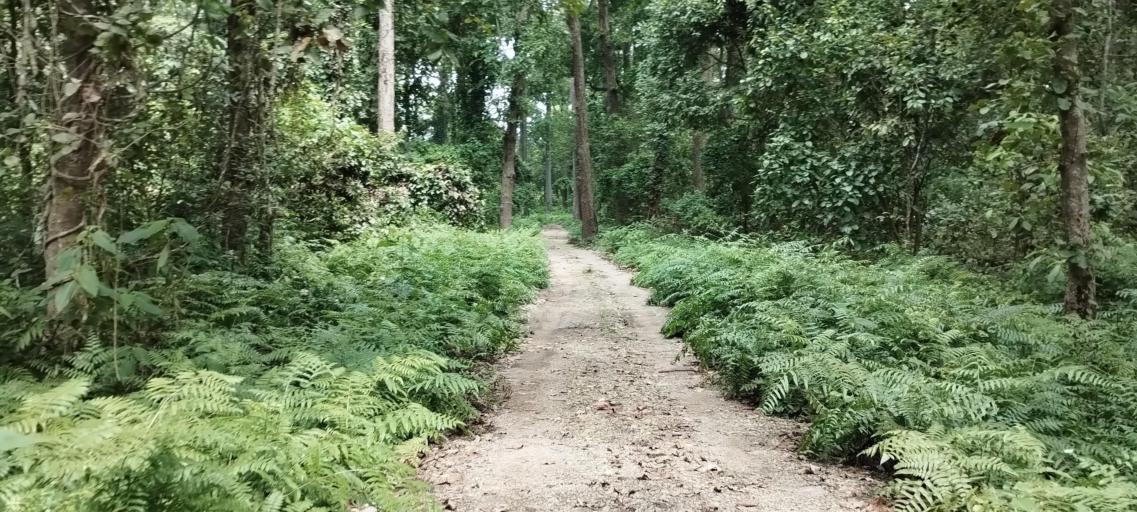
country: NP
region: Far Western
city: Tikapur
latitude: 28.4841
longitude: 81.2512
